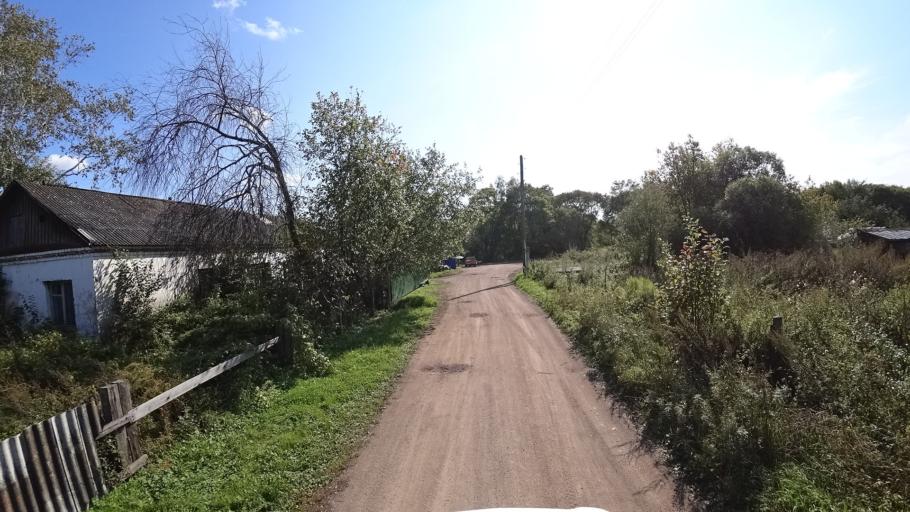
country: RU
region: Amur
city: Arkhara
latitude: 49.4004
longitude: 130.1479
